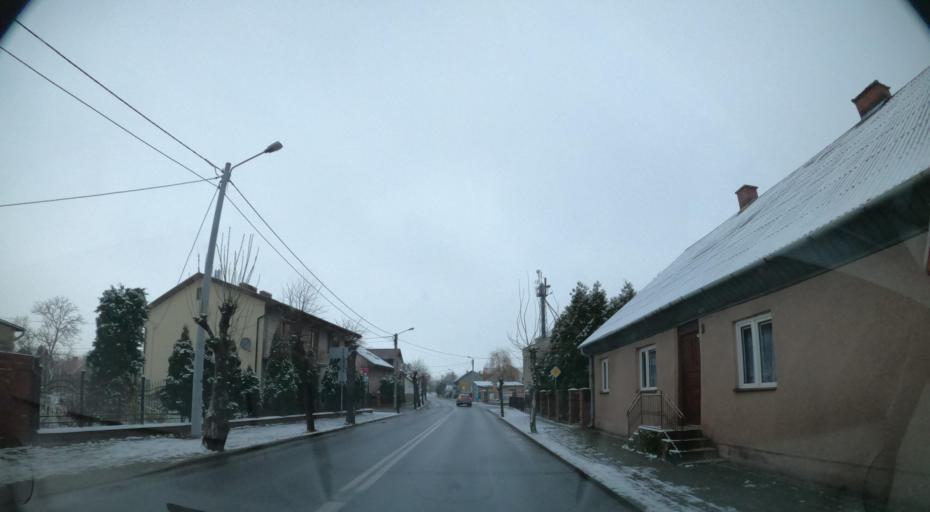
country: PL
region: Kujawsko-Pomorskie
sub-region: Powiat lipnowski
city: Dobrzyn nad Wisla
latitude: 52.6378
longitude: 19.3187
